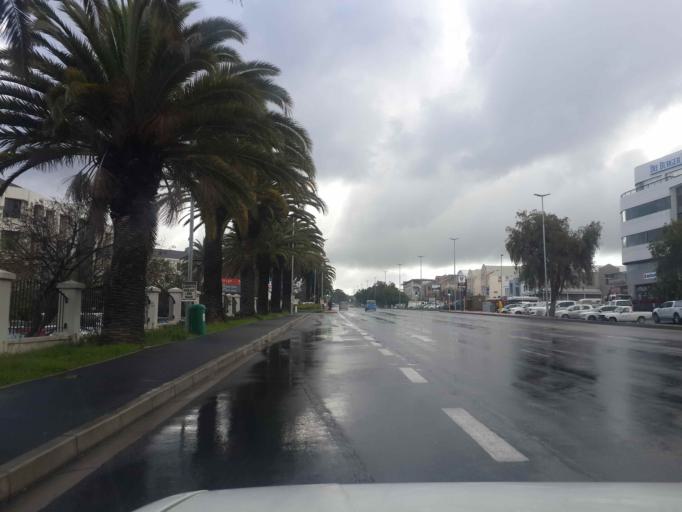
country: ZA
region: Western Cape
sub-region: City of Cape Town
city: Kraaifontein
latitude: -33.8808
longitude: 18.6353
